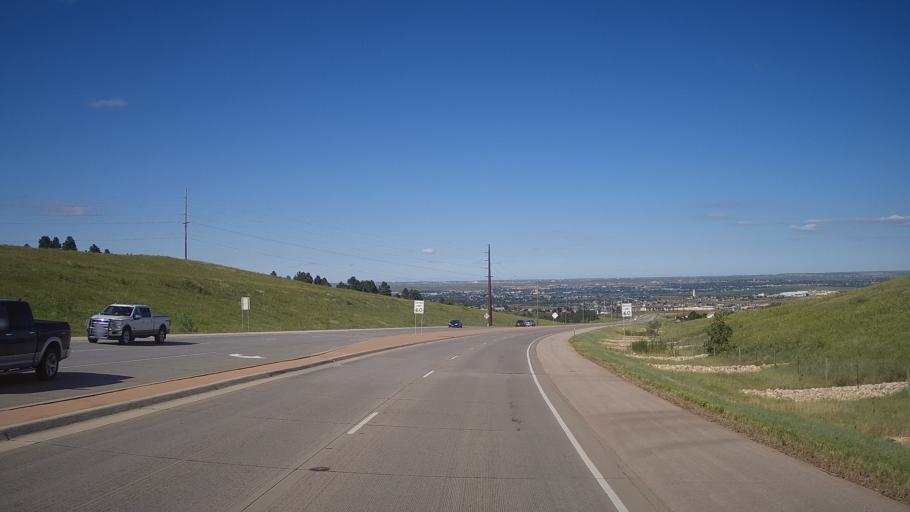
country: US
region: South Dakota
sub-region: Pennington County
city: Rapid City
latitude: 44.0217
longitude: -103.2413
